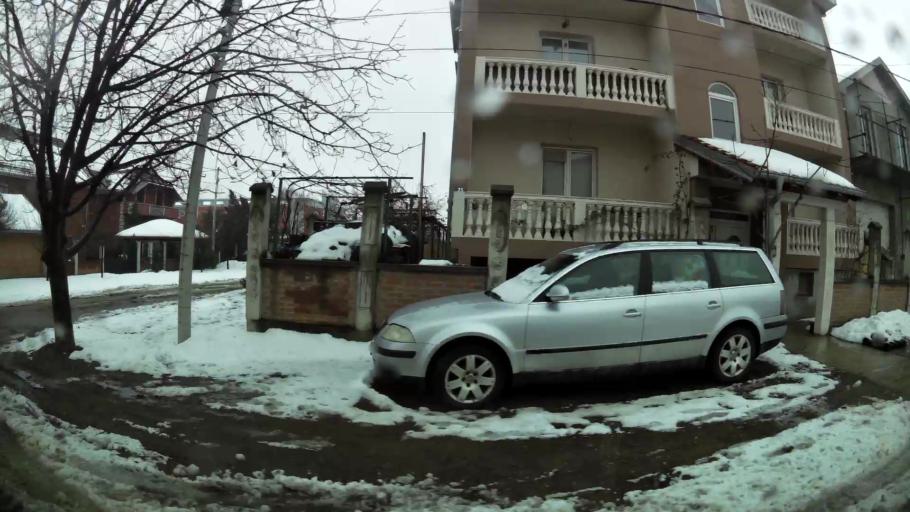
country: RS
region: Central Serbia
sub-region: Belgrade
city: Zemun
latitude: 44.8554
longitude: 20.3492
